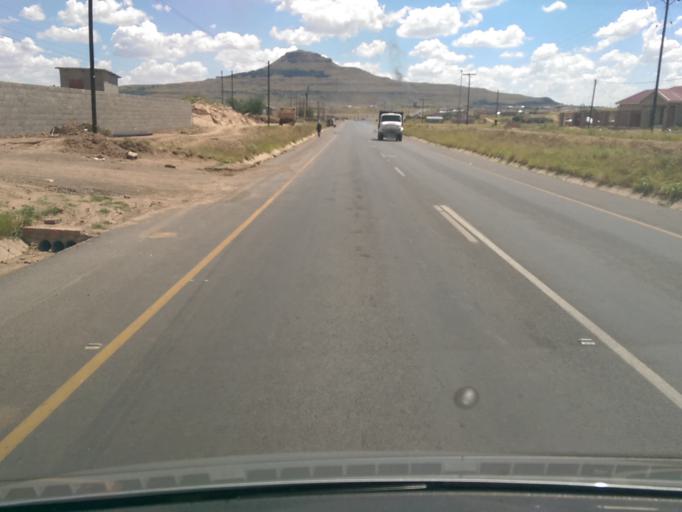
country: LS
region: Maseru
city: Maseru
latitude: -29.3766
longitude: 27.4910
